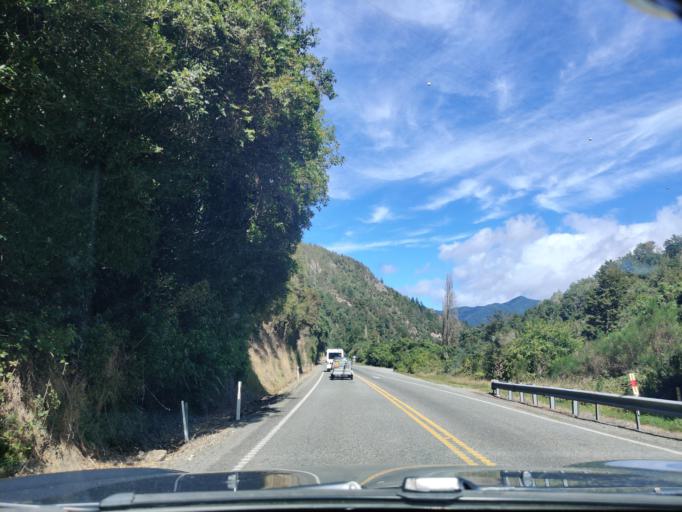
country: NZ
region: West Coast
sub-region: Buller District
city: Westport
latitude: -41.7694
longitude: 172.2305
